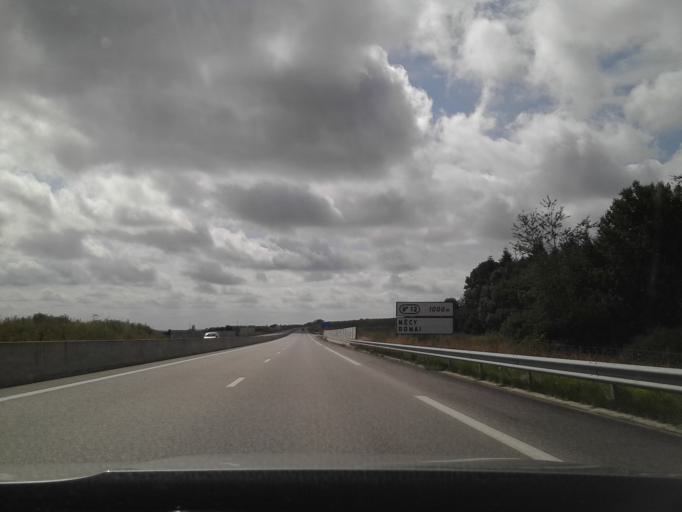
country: FR
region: Lower Normandy
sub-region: Departement du Calvados
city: Falaise
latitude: 48.8328
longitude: -0.1489
